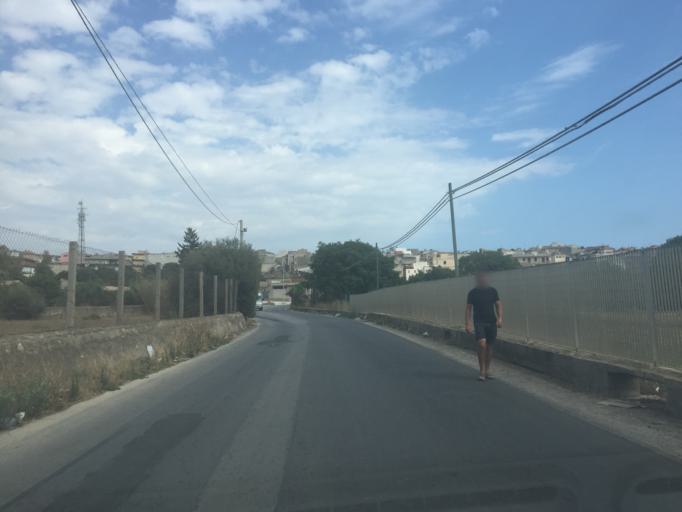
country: IT
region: Sicily
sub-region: Ragusa
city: Santa Croce Camerina
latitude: 36.8310
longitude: 14.5195
